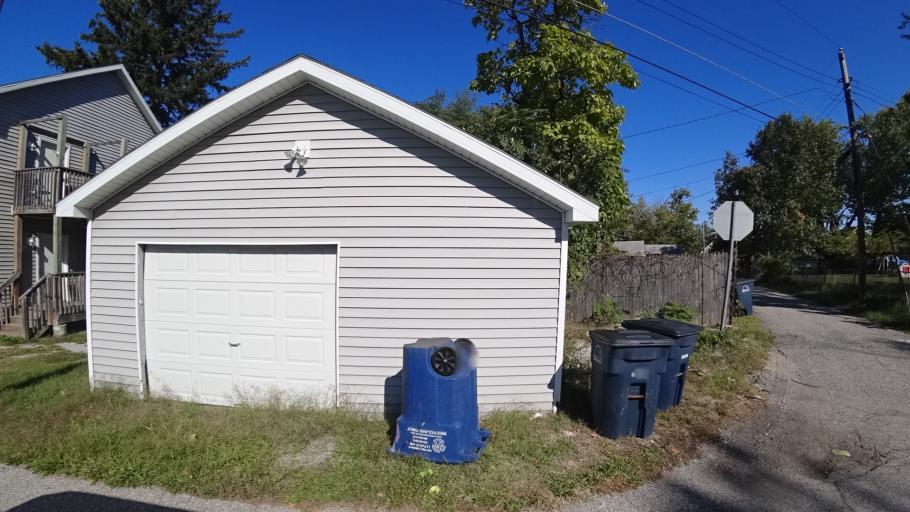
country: US
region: Indiana
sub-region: LaPorte County
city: Michigan City
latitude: 41.7026
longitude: -86.9138
